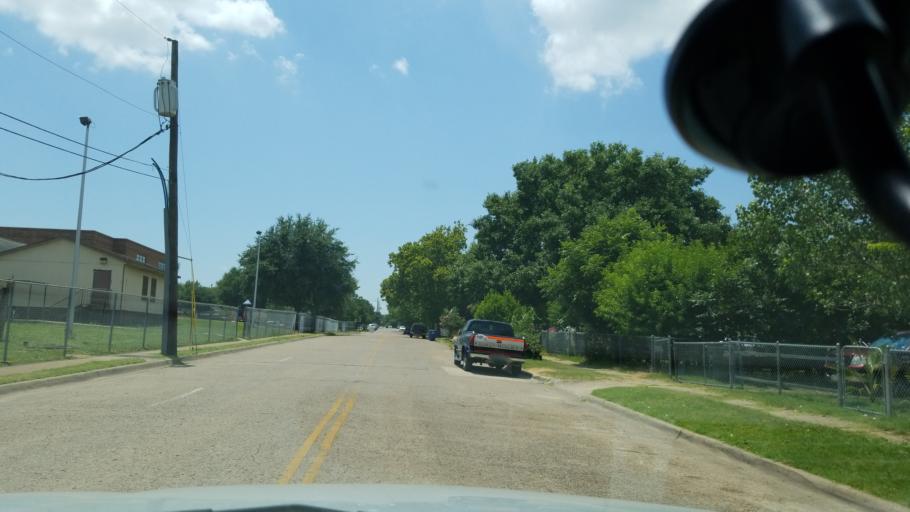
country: US
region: Texas
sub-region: Dallas County
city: Cockrell Hill
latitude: 32.7288
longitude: -96.8692
